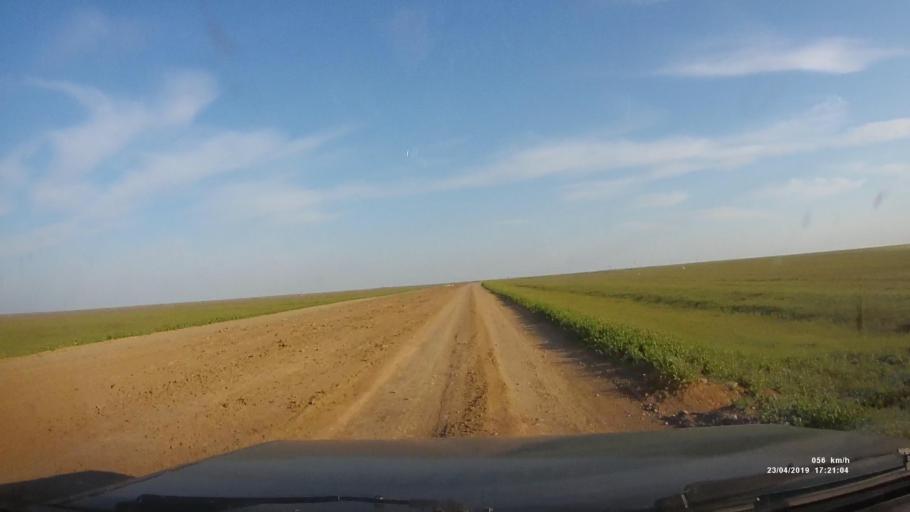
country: RU
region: Kalmykiya
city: Priyutnoye
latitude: 46.1789
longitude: 43.5036
